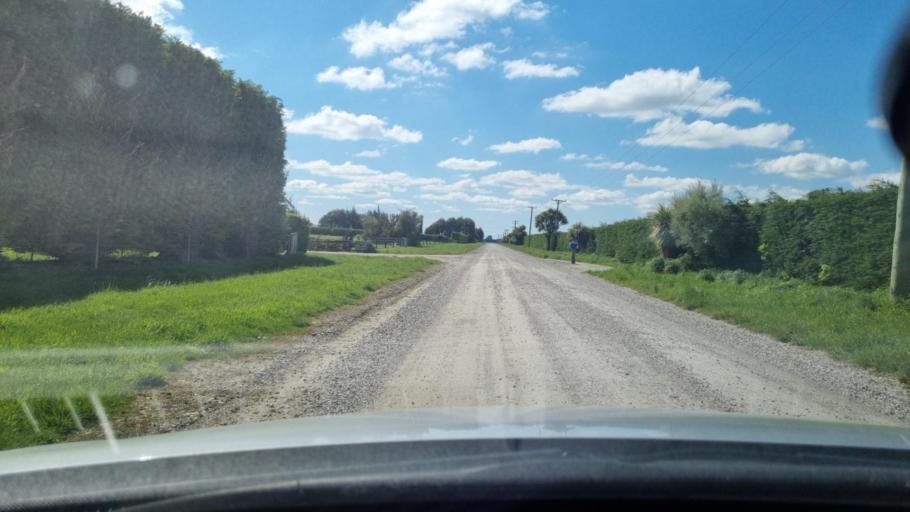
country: NZ
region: Southland
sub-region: Invercargill City
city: Invercargill
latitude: -46.3756
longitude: 168.2985
